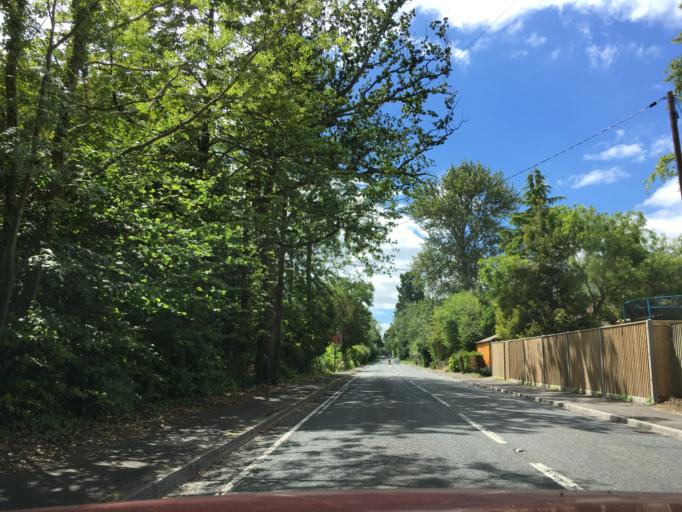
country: GB
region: England
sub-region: Hampshire
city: Highclere
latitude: 51.3434
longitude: -1.3727
